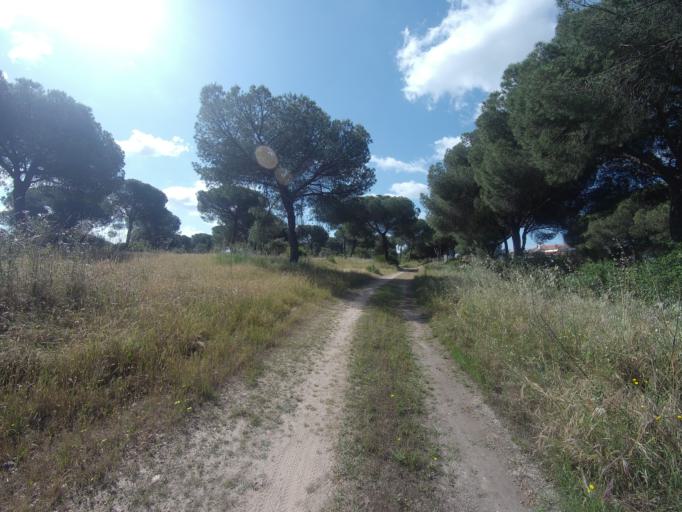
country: ES
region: Andalusia
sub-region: Provincia de Huelva
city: Aljaraque
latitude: 37.2433
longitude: -7.0304
